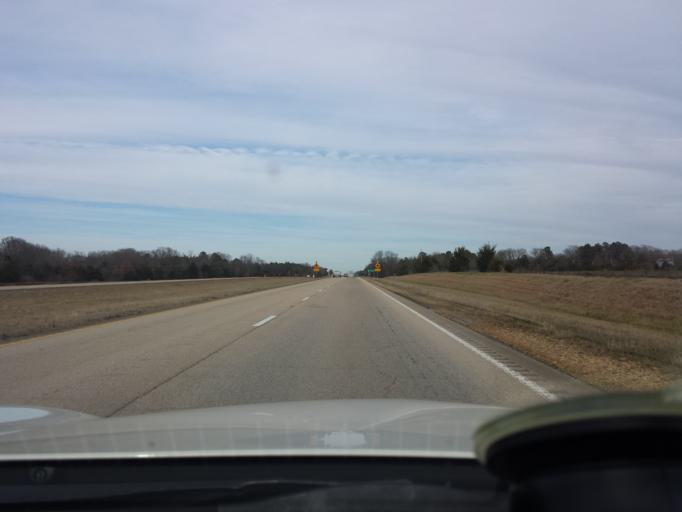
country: US
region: Mississippi
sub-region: Chickasaw County
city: Okolona
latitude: 33.9684
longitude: -88.7104
